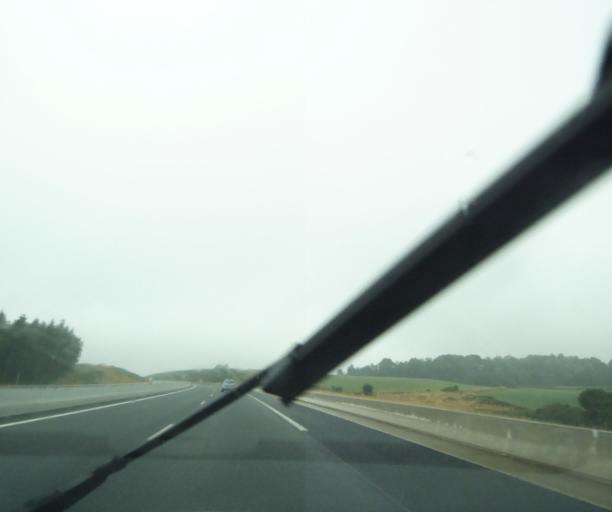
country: FR
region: Midi-Pyrenees
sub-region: Departement de l'Aveyron
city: Naucelle
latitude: 44.2150
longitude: 2.4066
